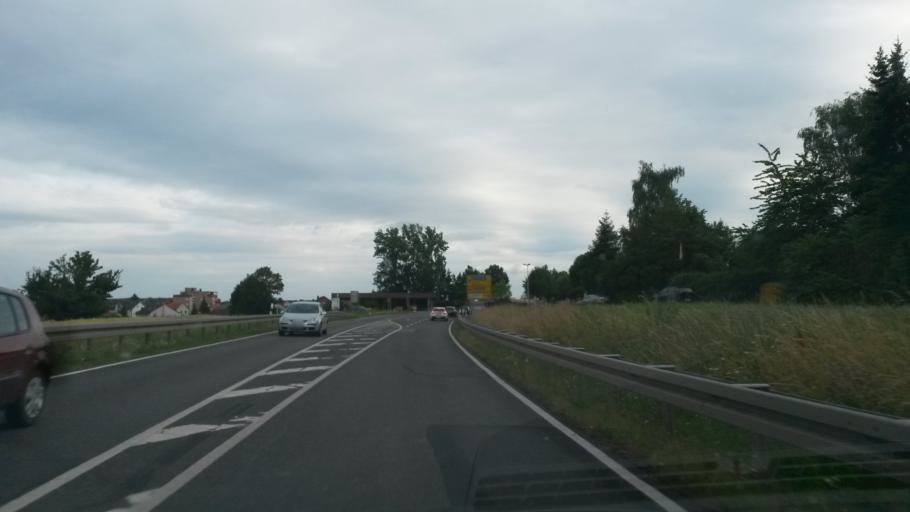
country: DE
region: Bavaria
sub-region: Regierungsbezirk Unterfranken
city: Waldbuttelbrunn
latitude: 49.7947
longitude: 9.8489
